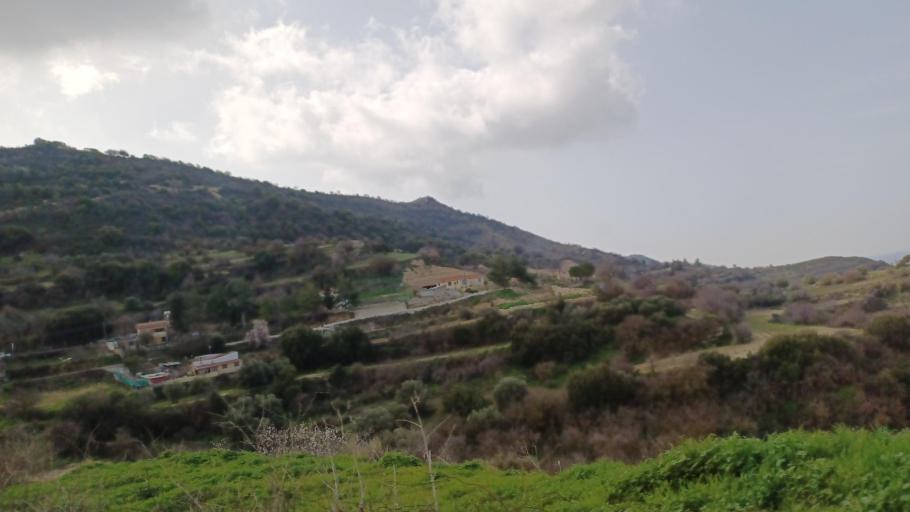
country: CY
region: Limassol
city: Pachna
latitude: 34.7811
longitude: 32.7363
